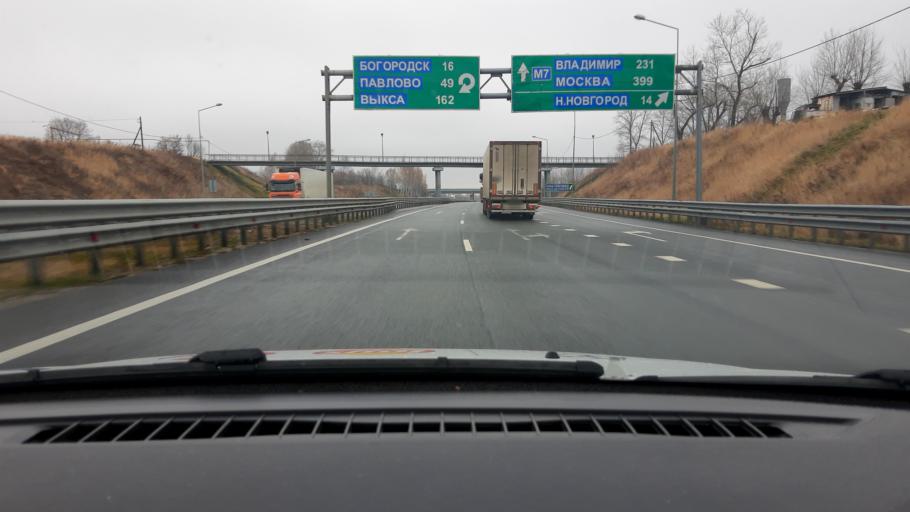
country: RU
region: Nizjnij Novgorod
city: Burevestnik
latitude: 56.1683
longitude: 43.7489
